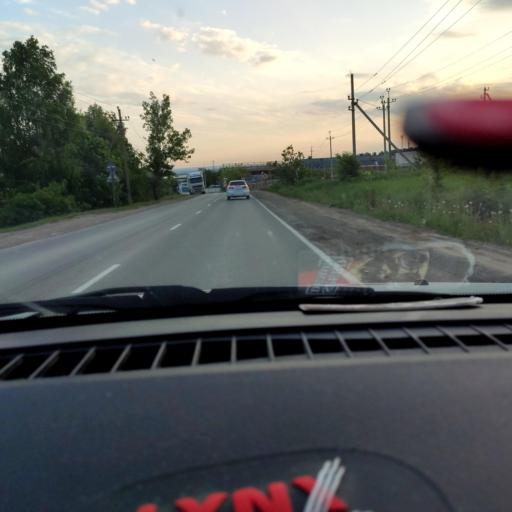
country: RU
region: Perm
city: Ferma
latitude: 57.9129
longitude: 56.3105
